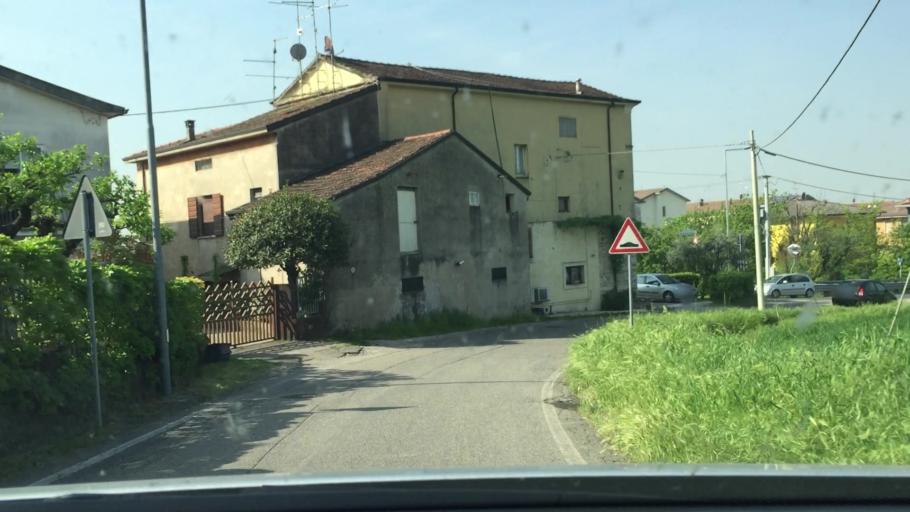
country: IT
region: Veneto
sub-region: Provincia di Verona
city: Monticelli-Fontana
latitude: 45.4243
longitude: 11.1188
